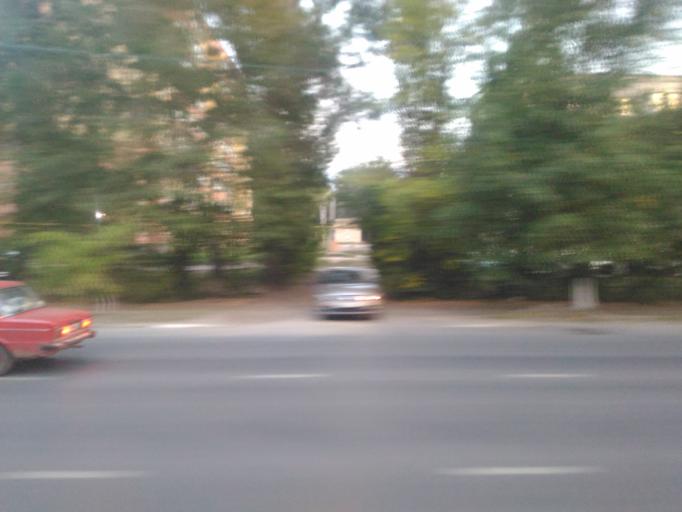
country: RU
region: Ulyanovsk
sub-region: Ulyanovskiy Rayon
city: Ulyanovsk
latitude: 54.2899
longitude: 48.3075
